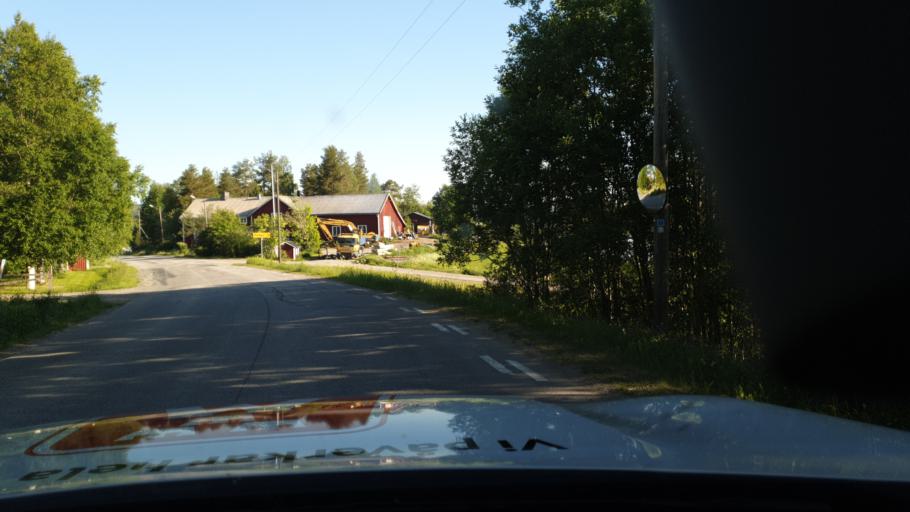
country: SE
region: Vaesterbotten
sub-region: Umea Kommun
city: Roback
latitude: 64.0322
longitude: 20.0840
